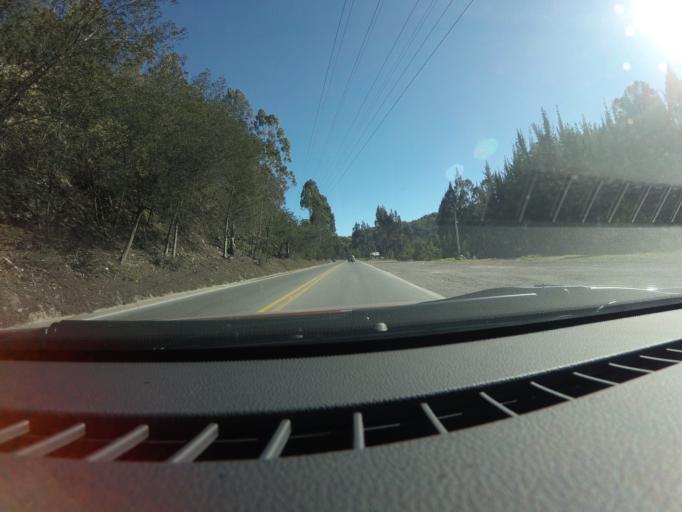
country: CO
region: Cundinamarca
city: Sutatausa
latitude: 5.2538
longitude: -73.8519
